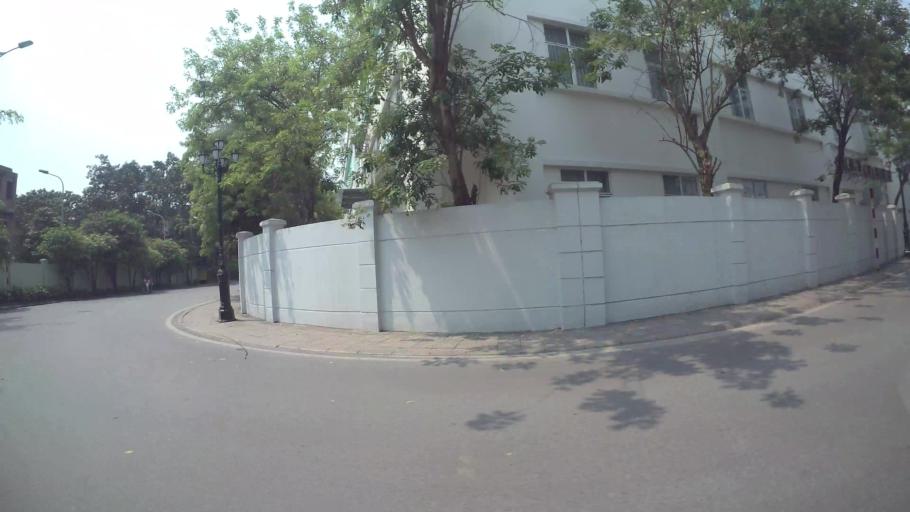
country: VN
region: Ha Noi
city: Thanh Xuan
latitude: 21.0011
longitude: 105.8150
